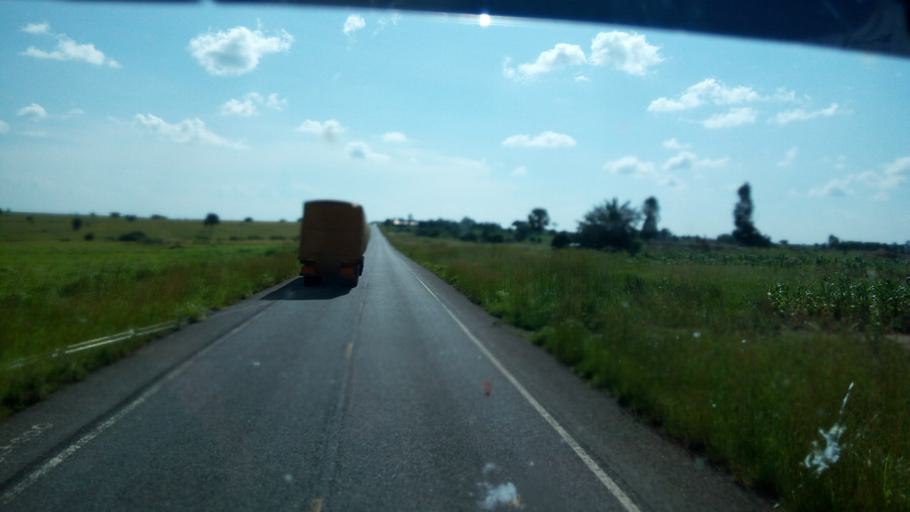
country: UG
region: Northern Region
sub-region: Nwoya District
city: Nwoya
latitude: 2.5648
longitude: 31.6450
